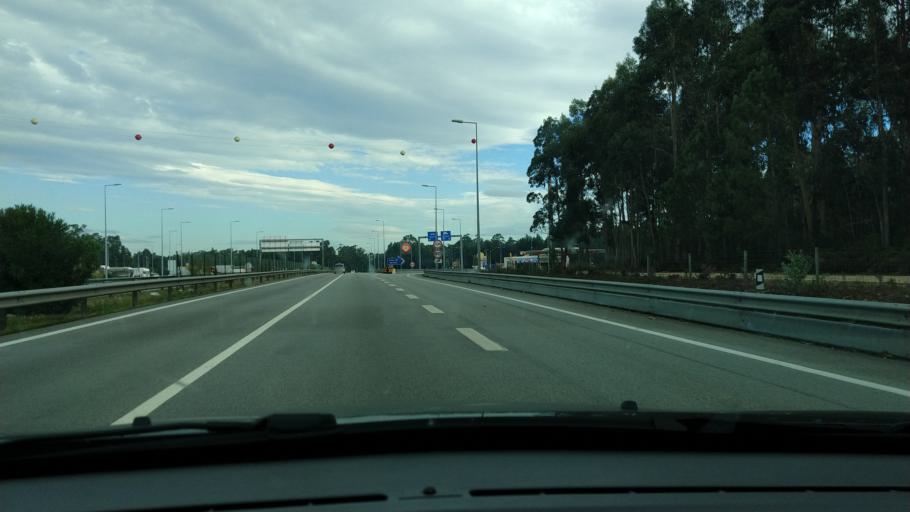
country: PT
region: Aveiro
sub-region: Aveiro
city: Eixo
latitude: 40.6583
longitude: -8.5924
